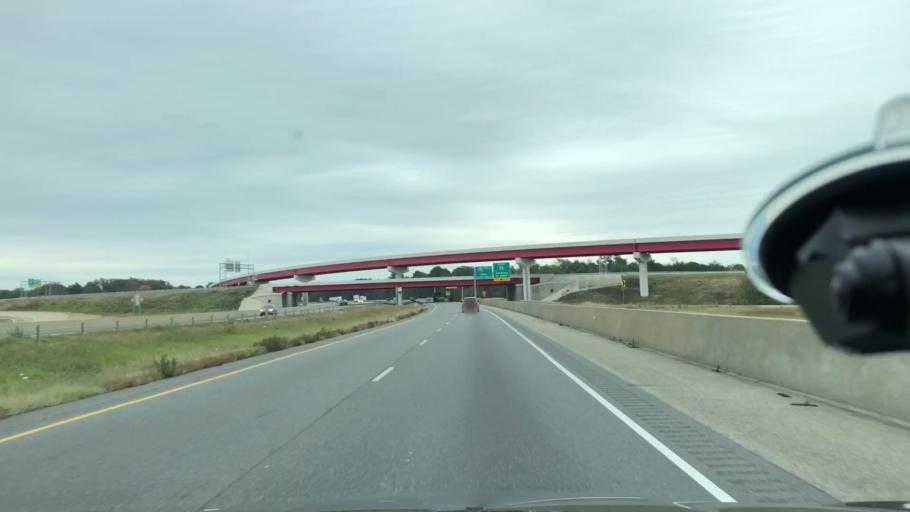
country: US
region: Arkansas
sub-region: Miller County
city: Texarkana
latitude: 33.4791
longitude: -93.9894
